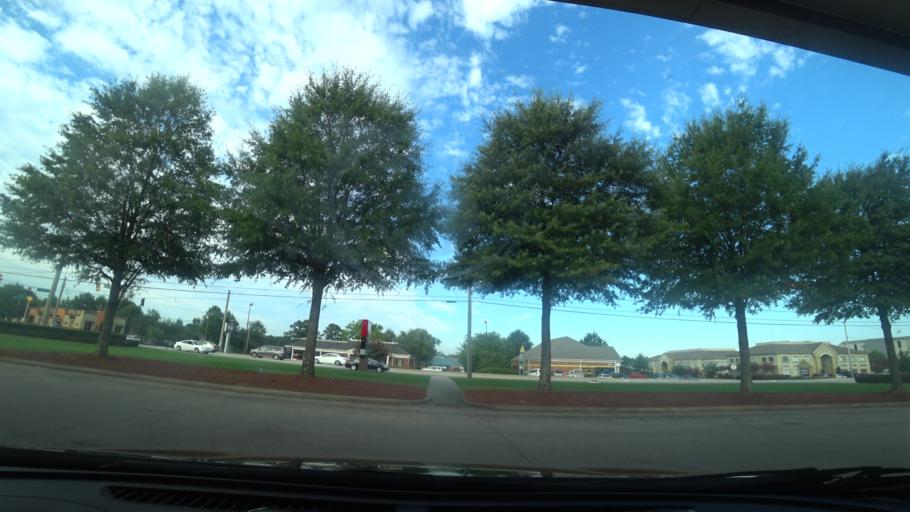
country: US
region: Georgia
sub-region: Rockdale County
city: Conyers
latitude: 33.6263
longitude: -83.9791
